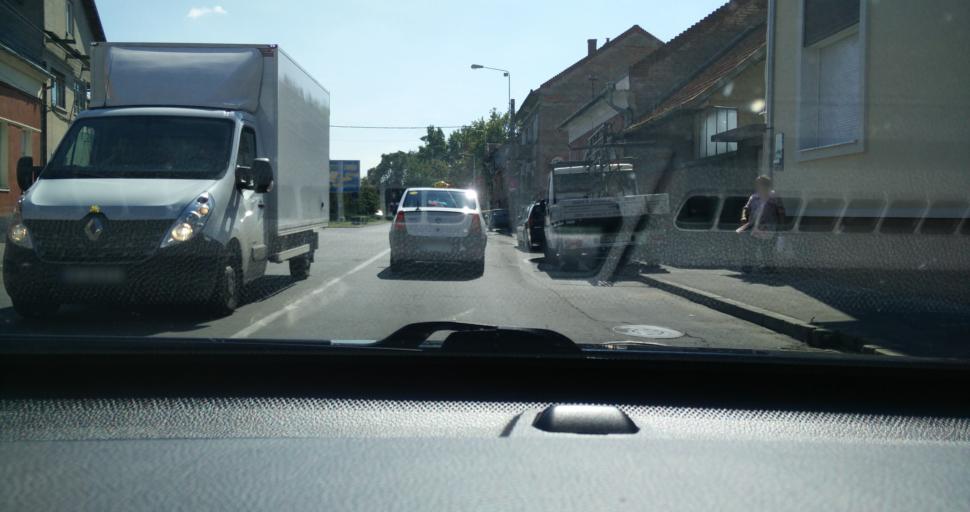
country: RO
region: Bihor
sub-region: Comuna Biharea
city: Oradea
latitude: 47.0498
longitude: 21.9277
